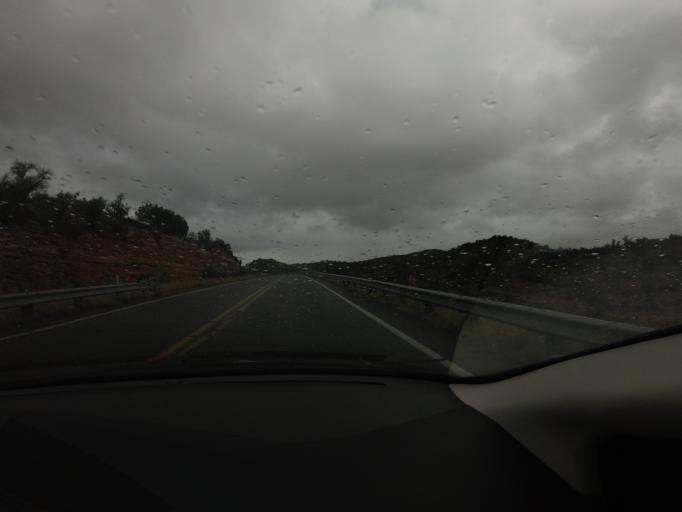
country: US
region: Arizona
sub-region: Yavapai County
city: Cornville
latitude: 34.7017
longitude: -111.8687
